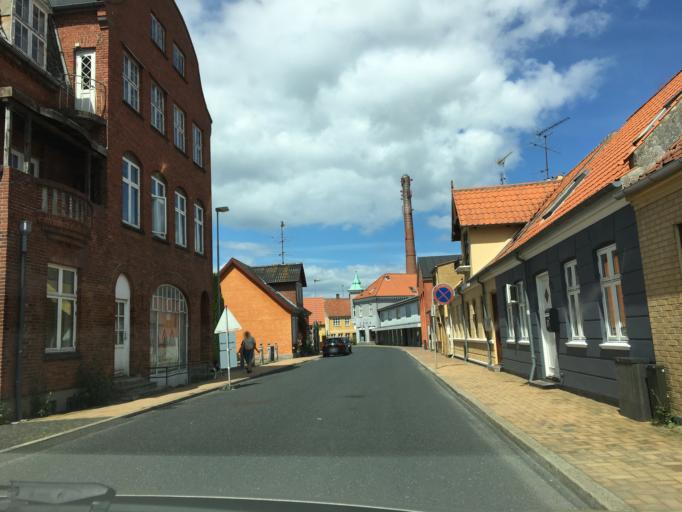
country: DK
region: South Denmark
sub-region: Langeland Kommune
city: Rudkobing
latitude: 54.9376
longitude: 10.7160
